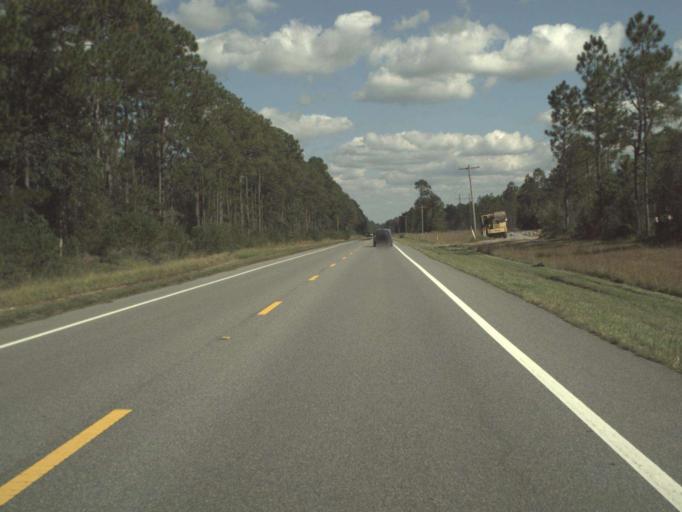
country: US
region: Florida
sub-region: Walton County
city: Freeport
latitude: 30.4750
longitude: -86.0050
